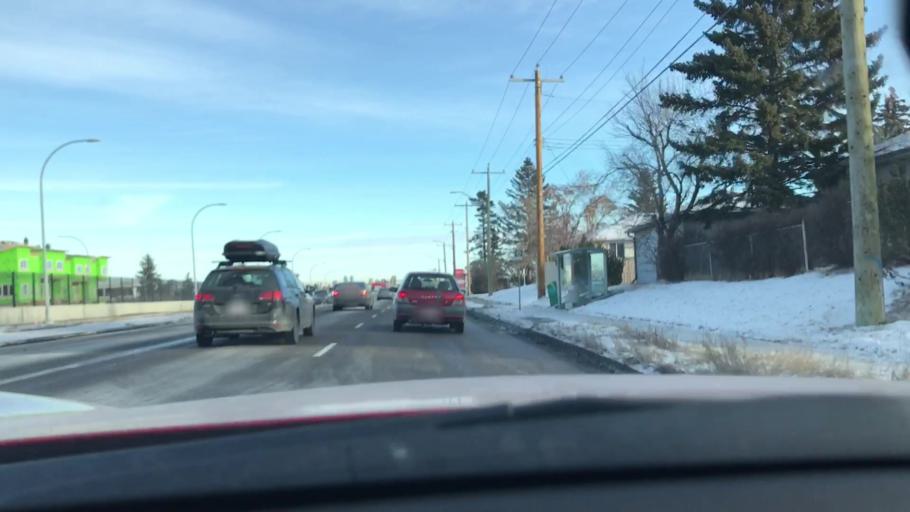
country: CA
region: Alberta
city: Calgary
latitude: 51.0378
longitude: -114.1468
